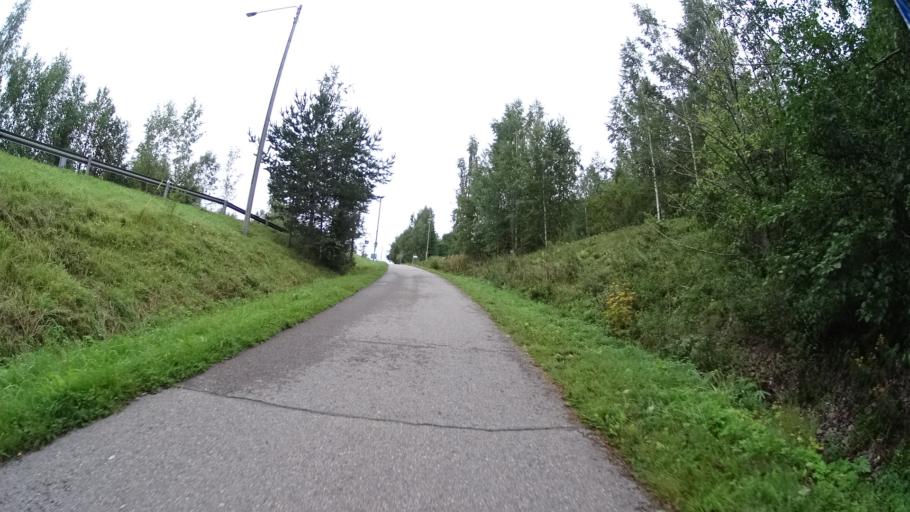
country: FI
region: Uusimaa
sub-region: Helsinki
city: Espoo
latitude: 60.2234
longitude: 24.6606
